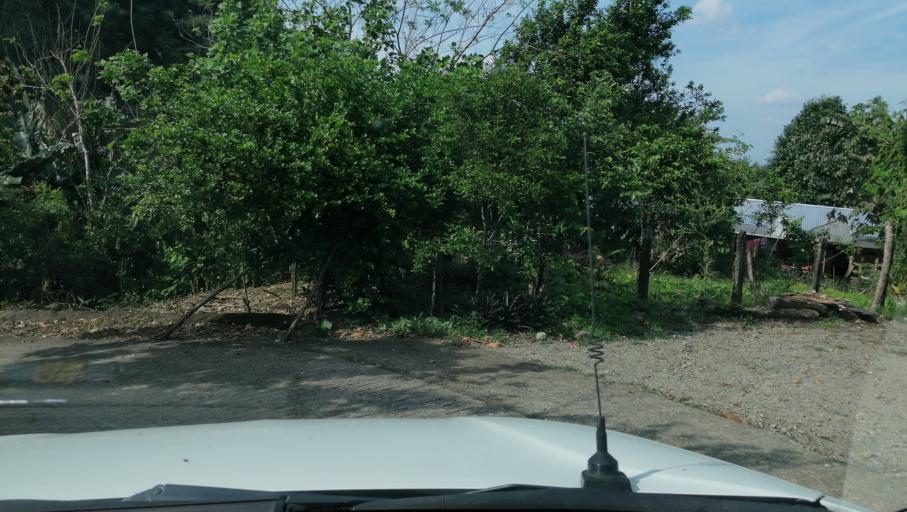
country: MX
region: Chiapas
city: Ostuacan
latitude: 17.4520
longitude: -93.2440
